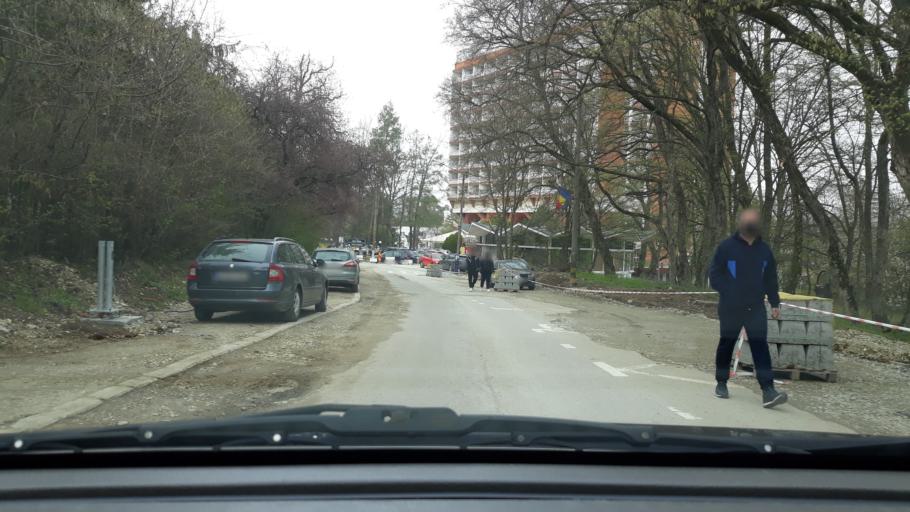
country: RO
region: Bihor
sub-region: Comuna Sanmartin
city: Sanmartin
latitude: 46.9907
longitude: 21.9762
